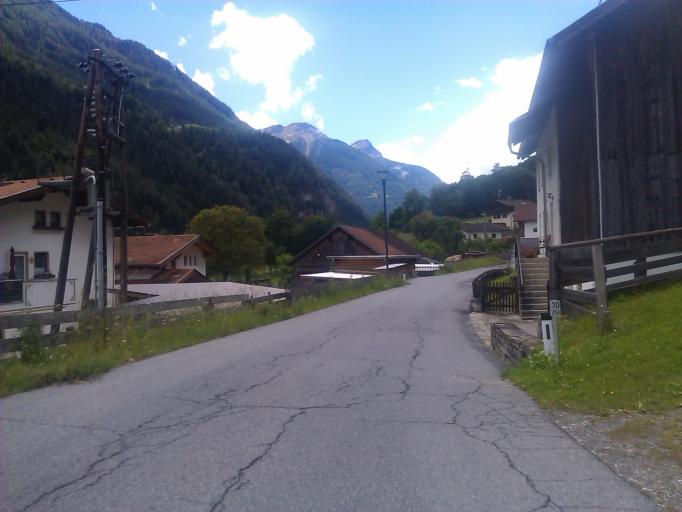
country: AT
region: Tyrol
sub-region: Politischer Bezirk Landeck
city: Serfaus
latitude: 47.0025
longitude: 10.5889
